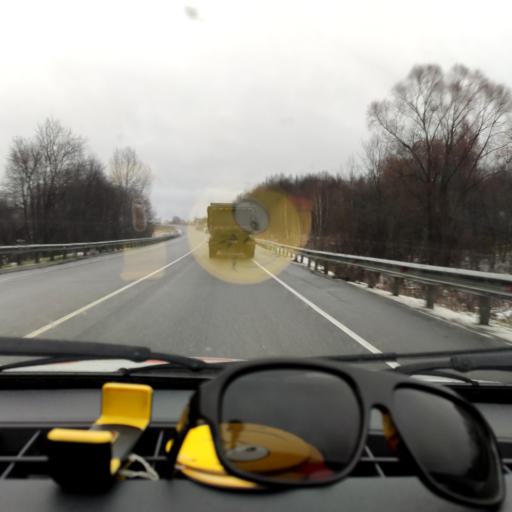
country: RU
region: Bashkortostan
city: Urman
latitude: 54.8175
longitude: 56.8638
